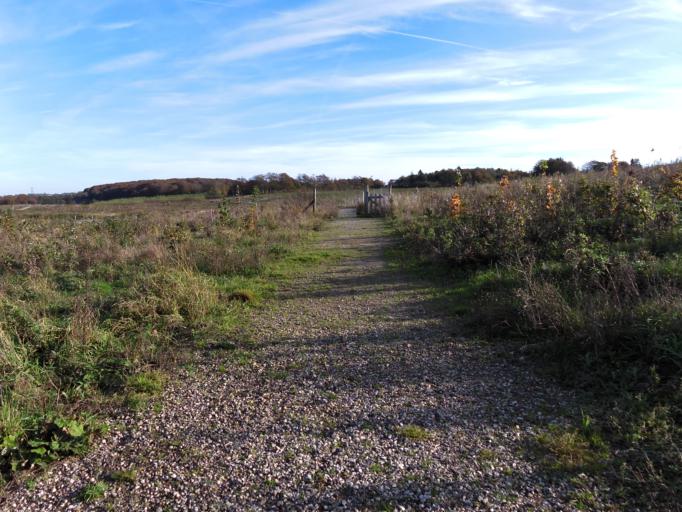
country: DK
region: Central Jutland
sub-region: Arhus Kommune
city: Framlev
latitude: 56.1265
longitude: 10.0173
